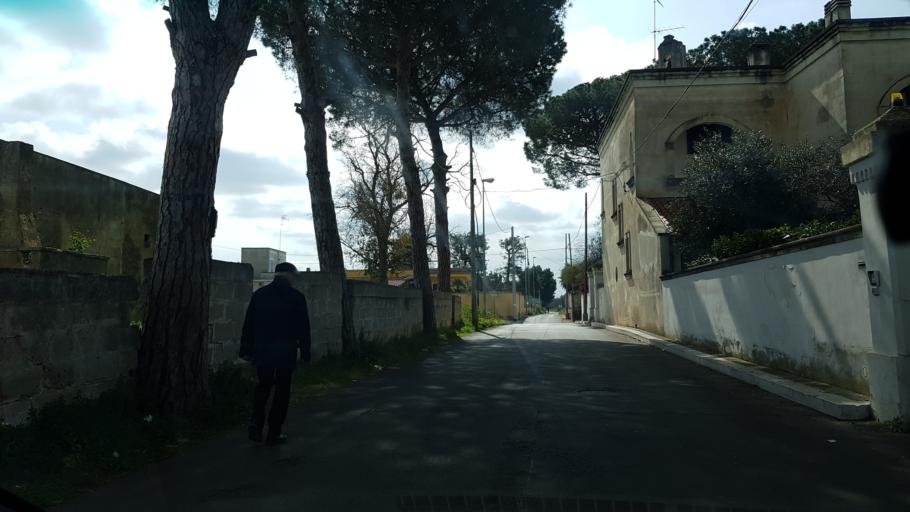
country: IT
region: Apulia
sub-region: Provincia di Lecce
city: Squinzano
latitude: 40.4274
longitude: 18.0443
